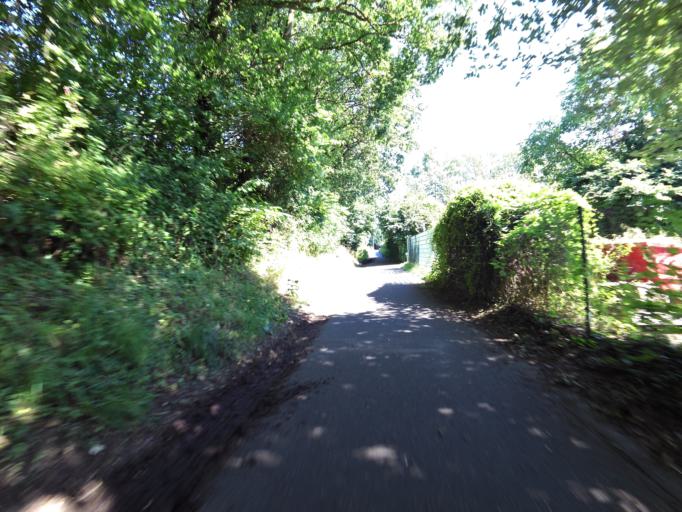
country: DE
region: North Rhine-Westphalia
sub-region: Regierungsbezirk Koln
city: Herzogenrath
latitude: 50.8642
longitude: 6.0915
